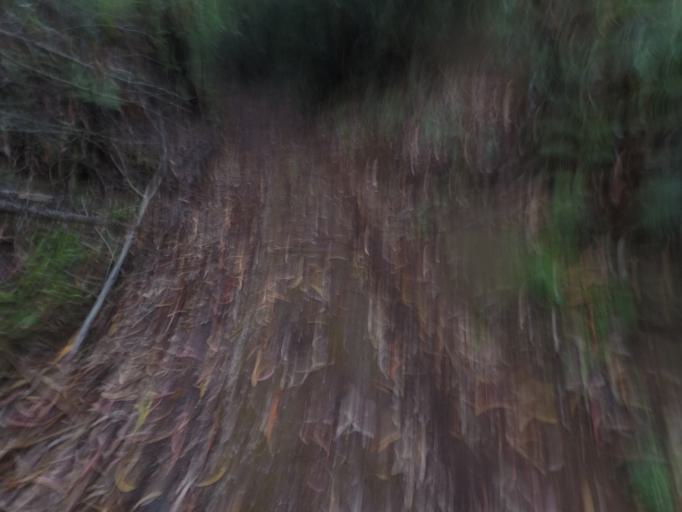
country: PT
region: Madeira
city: Ponta do Sol
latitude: 32.7111
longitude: -17.0931
